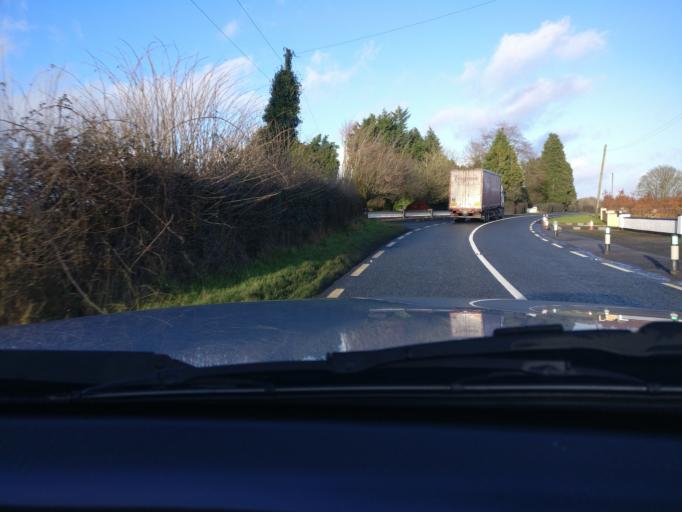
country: IE
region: Leinster
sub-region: An Iarmhi
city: Rathwire
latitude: 53.6196
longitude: -7.0859
